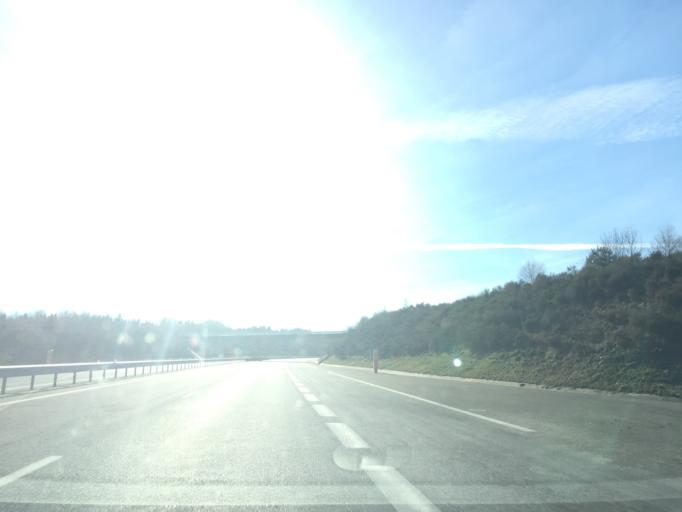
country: FR
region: Auvergne
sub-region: Departement du Puy-de-Dome
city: Gelles
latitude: 45.8035
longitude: 2.7676
